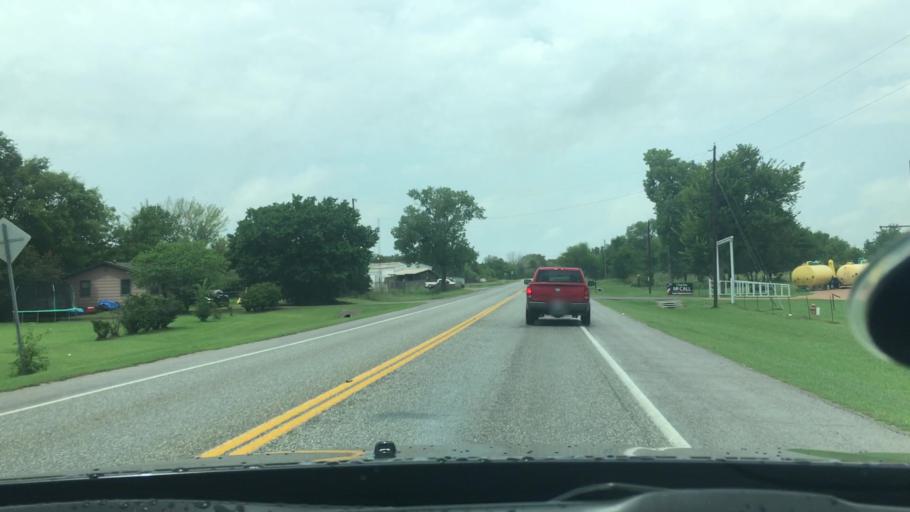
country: US
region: Oklahoma
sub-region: Johnston County
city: Tishomingo
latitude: 34.2460
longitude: -96.7546
